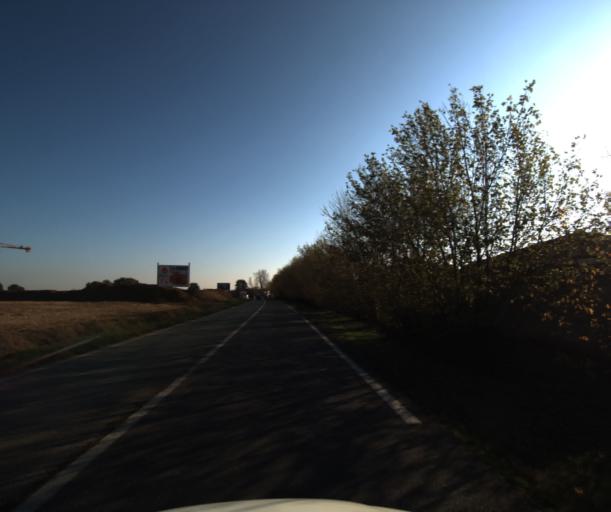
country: FR
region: Midi-Pyrenees
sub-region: Departement de la Haute-Garonne
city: Colomiers
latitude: 43.6267
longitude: 1.3317
